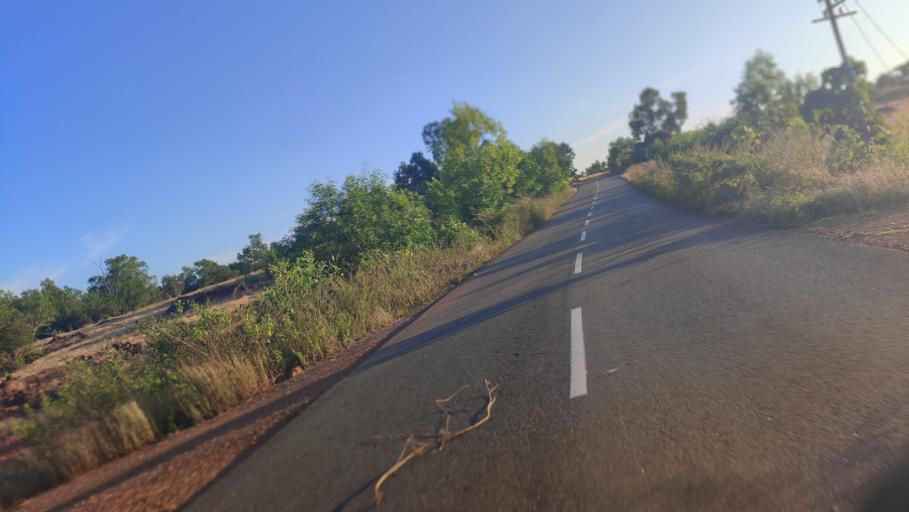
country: IN
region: Kerala
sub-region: Kasaragod District
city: Kasaragod
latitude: 12.4457
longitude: 75.0993
